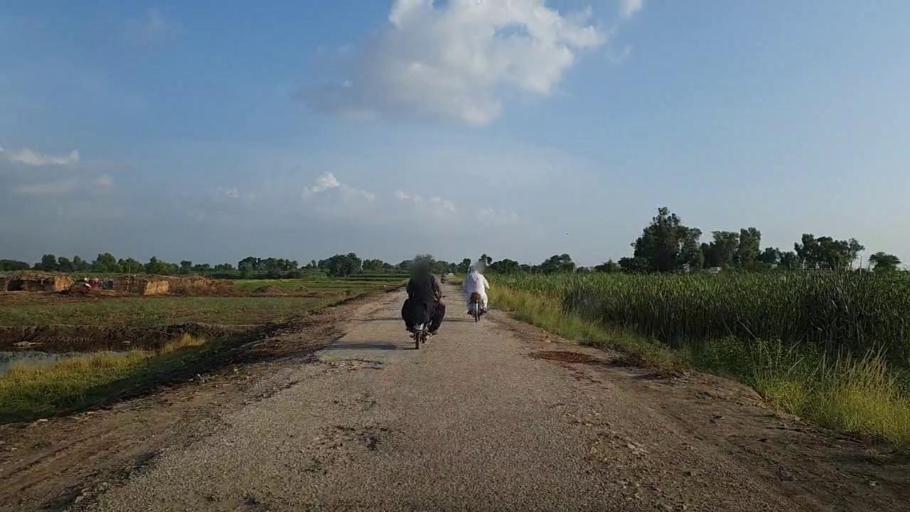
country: PK
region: Sindh
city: Hingorja
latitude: 27.0665
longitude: 68.4188
